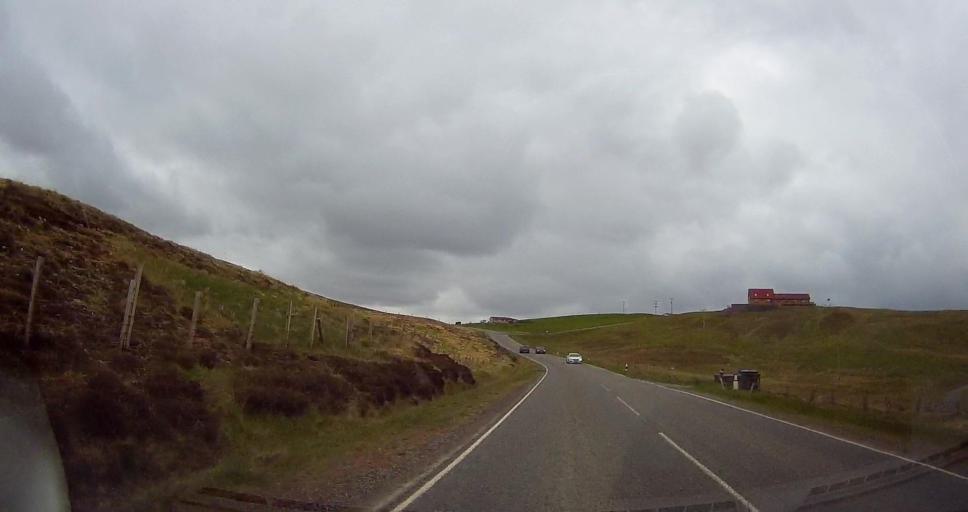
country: GB
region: Scotland
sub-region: Shetland Islands
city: Lerwick
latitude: 60.3833
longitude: -1.3424
